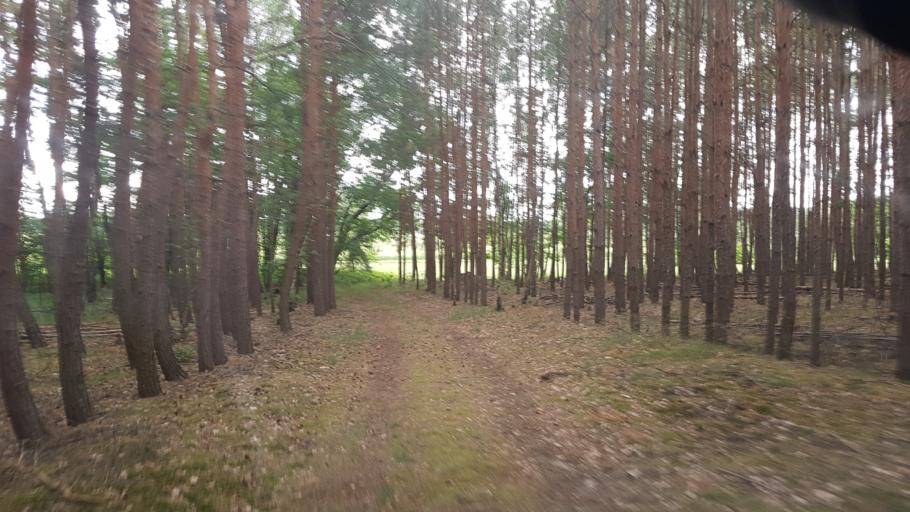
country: DE
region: Brandenburg
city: Finsterwalde
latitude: 51.6066
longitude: 13.6627
